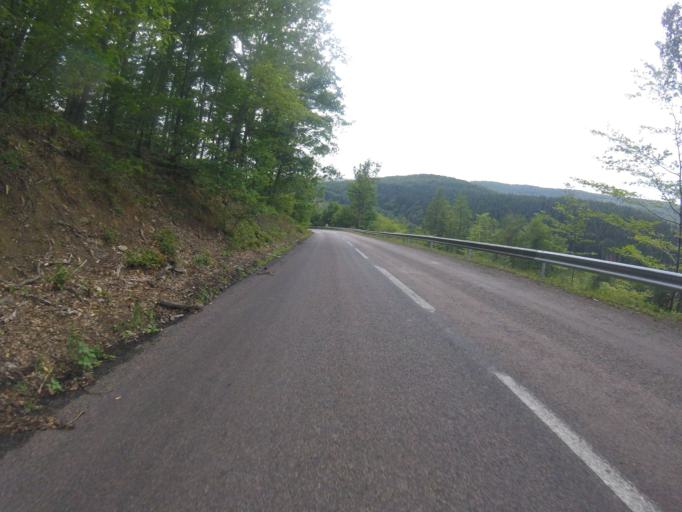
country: HU
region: Nograd
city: Batonyterenye
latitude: 47.8985
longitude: 19.8244
